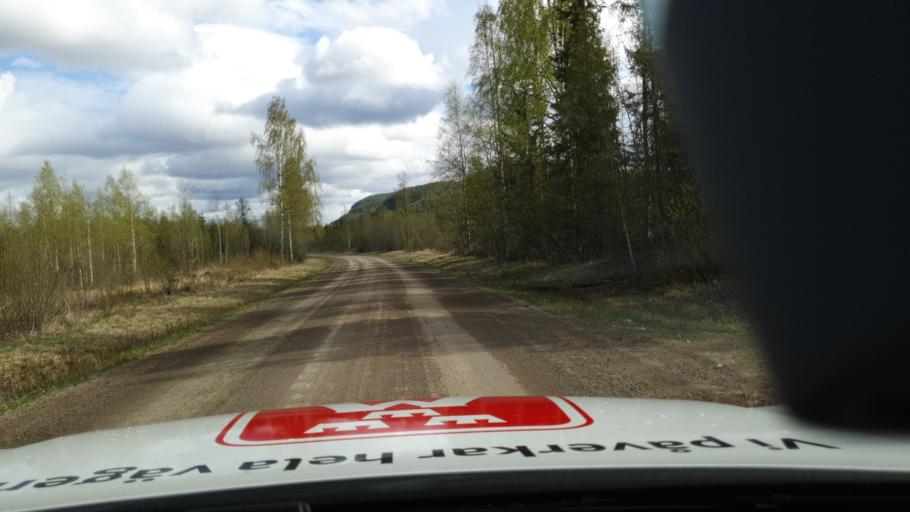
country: SE
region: Jaemtland
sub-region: Ragunda Kommun
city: Hammarstrand
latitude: 63.0869
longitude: 16.3348
